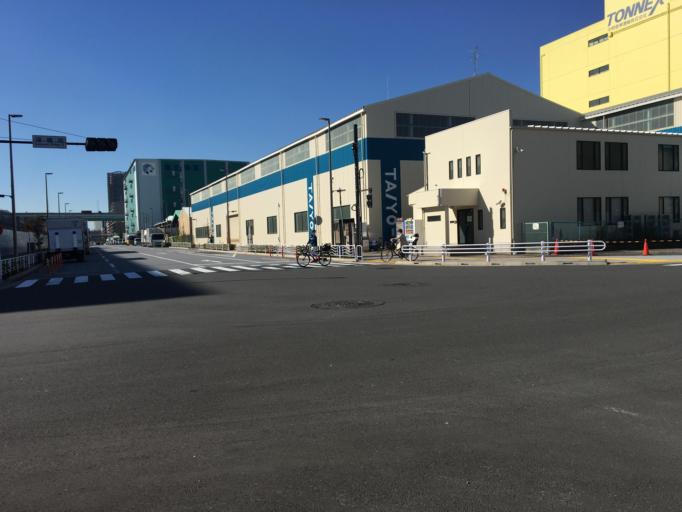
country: JP
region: Tokyo
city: Urayasu
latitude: 35.6526
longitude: 139.8159
